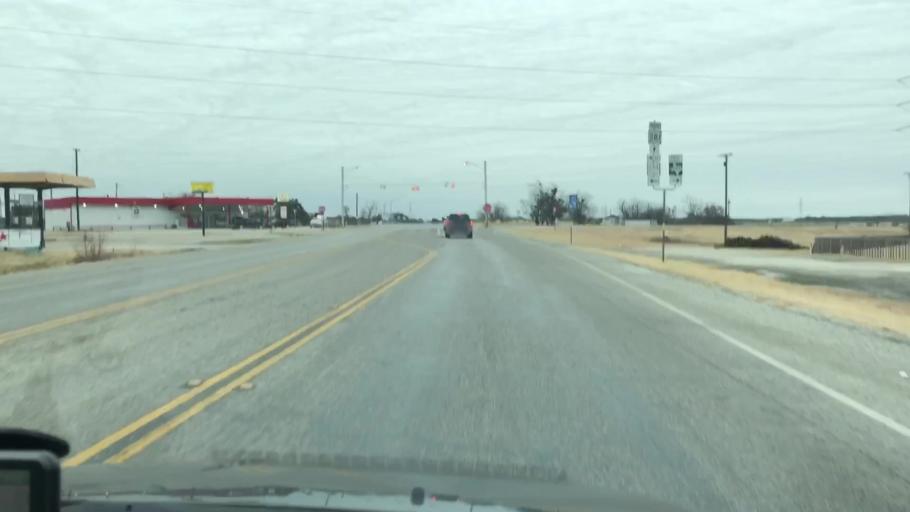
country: US
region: Texas
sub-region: Palo Pinto County
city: Mineral Wells
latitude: 32.9192
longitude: -98.0755
